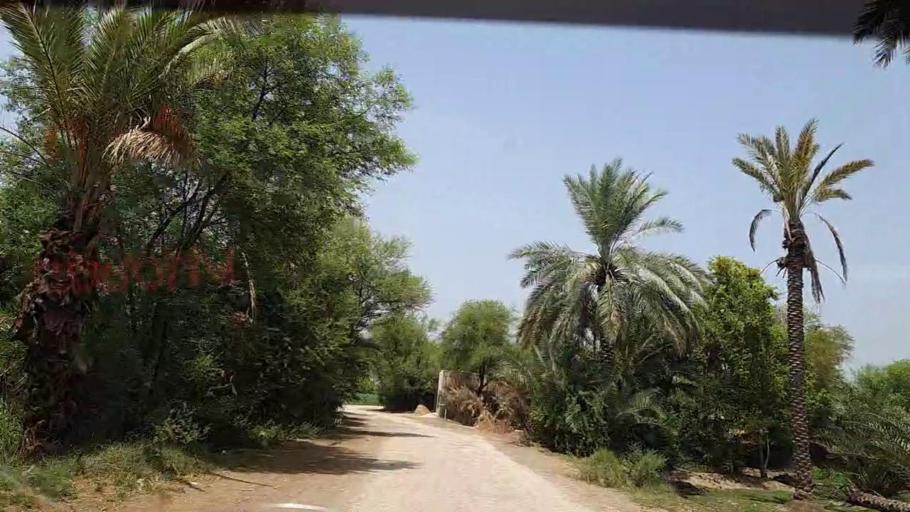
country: PK
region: Sindh
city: Ghotki
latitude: 28.0196
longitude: 69.3536
